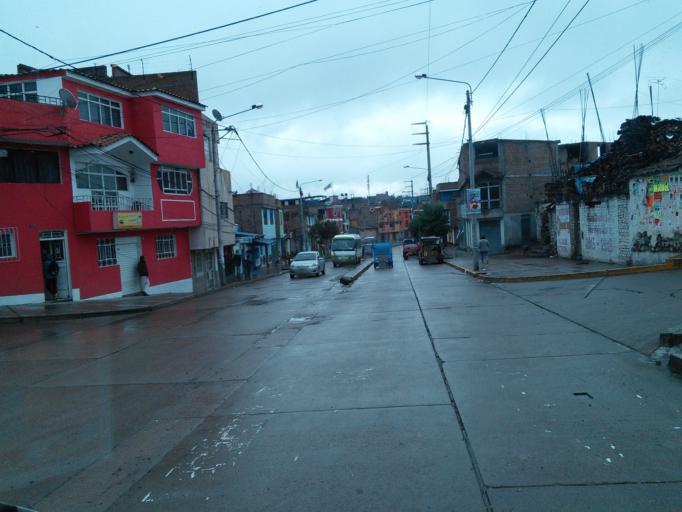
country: PE
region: Ayacucho
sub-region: Provincia de Huamanga
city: Ayacucho
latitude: -13.1662
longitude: -74.2249
